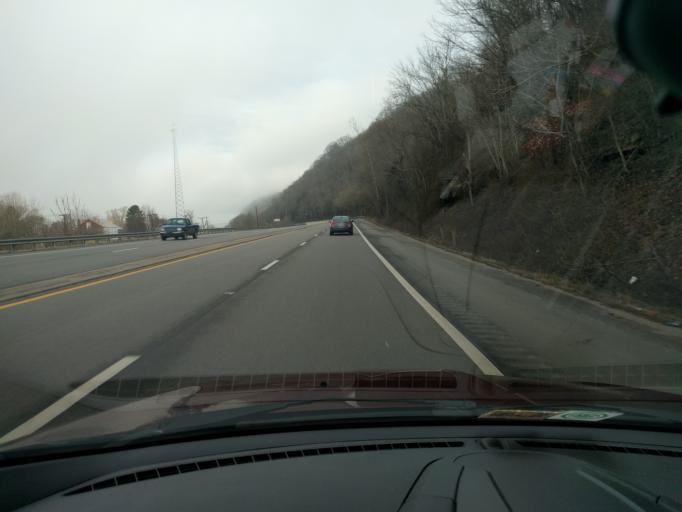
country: US
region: West Virginia
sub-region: Kanawha County
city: Belle
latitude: 38.2362
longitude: -81.5414
